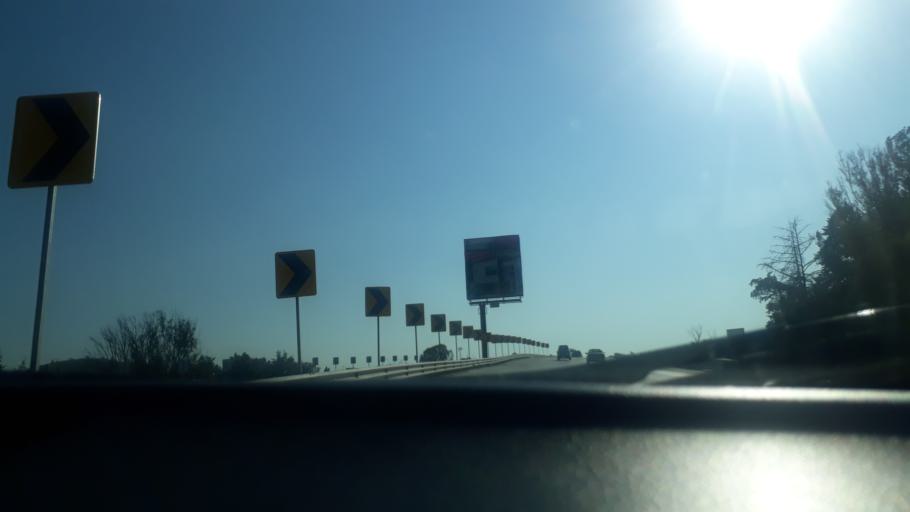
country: MX
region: Puebla
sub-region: Puebla
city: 18 de Marzo
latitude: 18.9737
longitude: -98.1902
